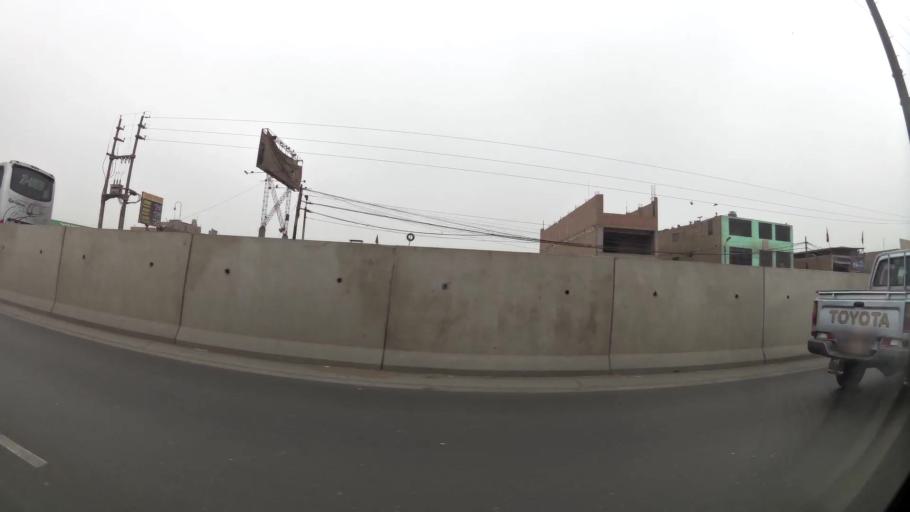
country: PE
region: Lima
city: Ventanilla
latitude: -11.8575
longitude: -77.0837
